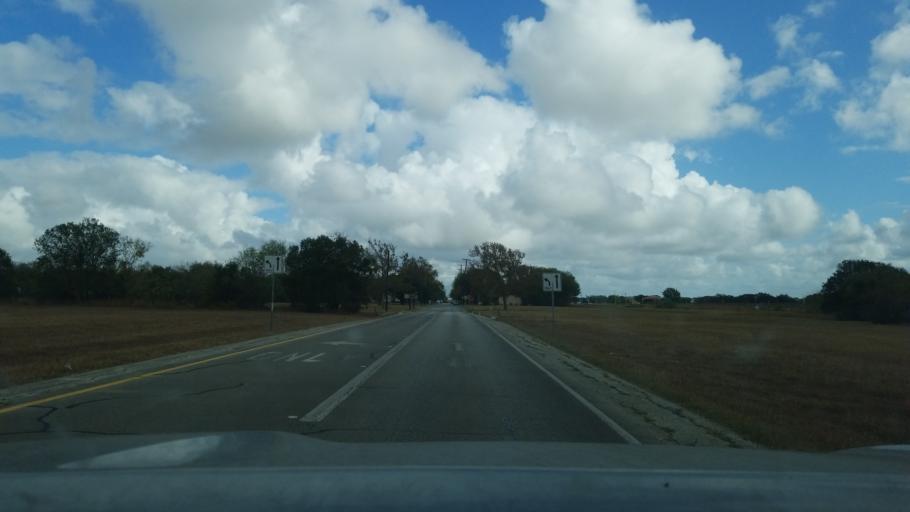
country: US
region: Texas
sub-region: Bexar County
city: Universal City
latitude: 29.5411
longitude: -98.2961
